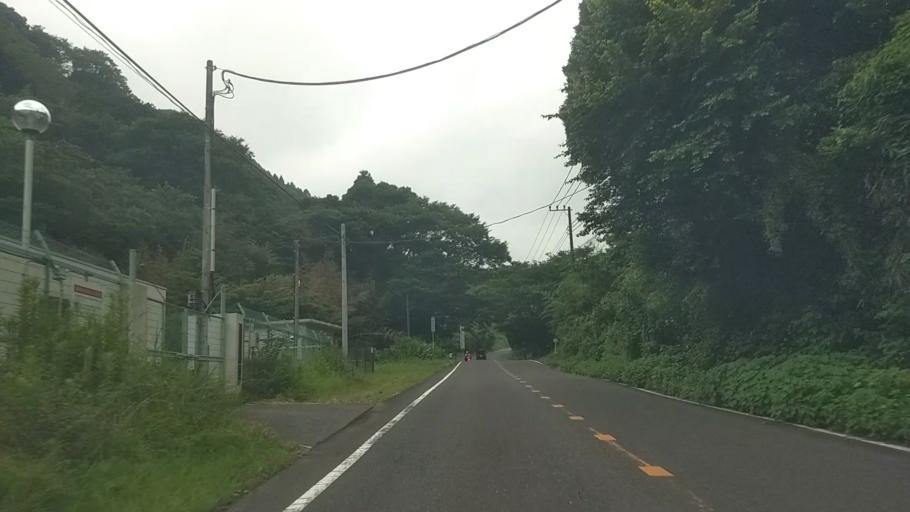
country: JP
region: Chiba
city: Kawaguchi
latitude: 35.1413
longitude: 139.9475
